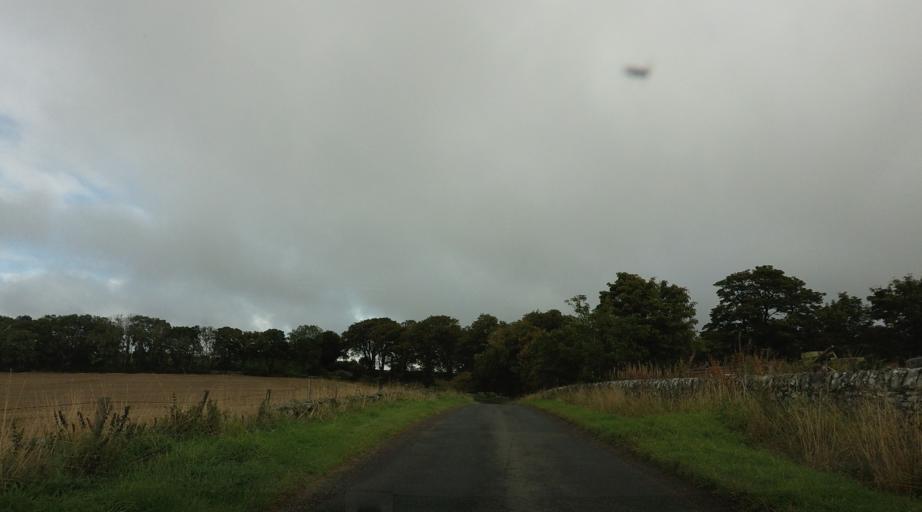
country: GB
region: Scotland
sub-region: Fife
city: Balmullo
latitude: 56.3611
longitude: -2.9736
